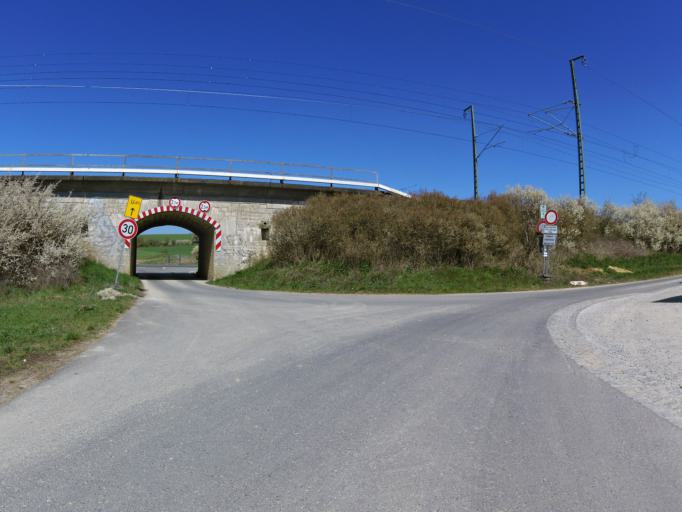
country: DE
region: Bavaria
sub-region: Regierungsbezirk Unterfranken
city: Rottendorf
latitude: 49.8011
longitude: 10.0383
